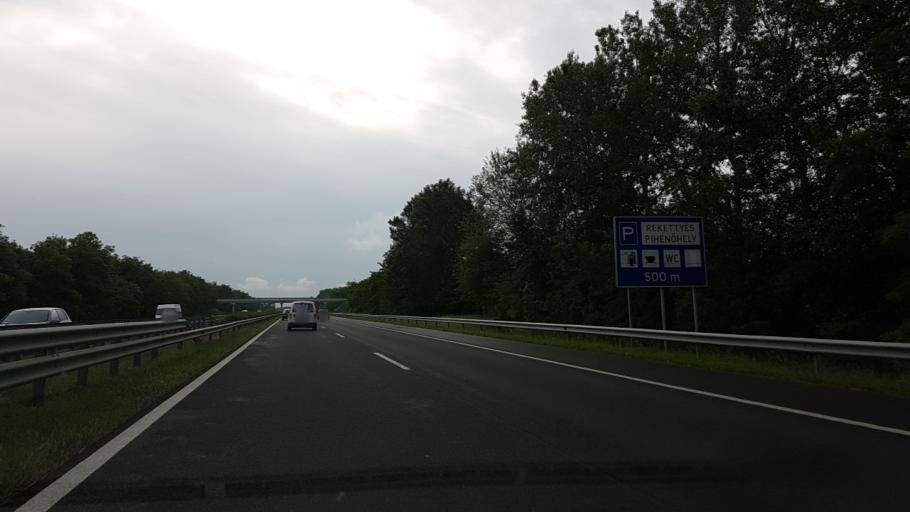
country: HU
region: Heves
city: Kal
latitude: 47.7225
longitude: 20.3009
